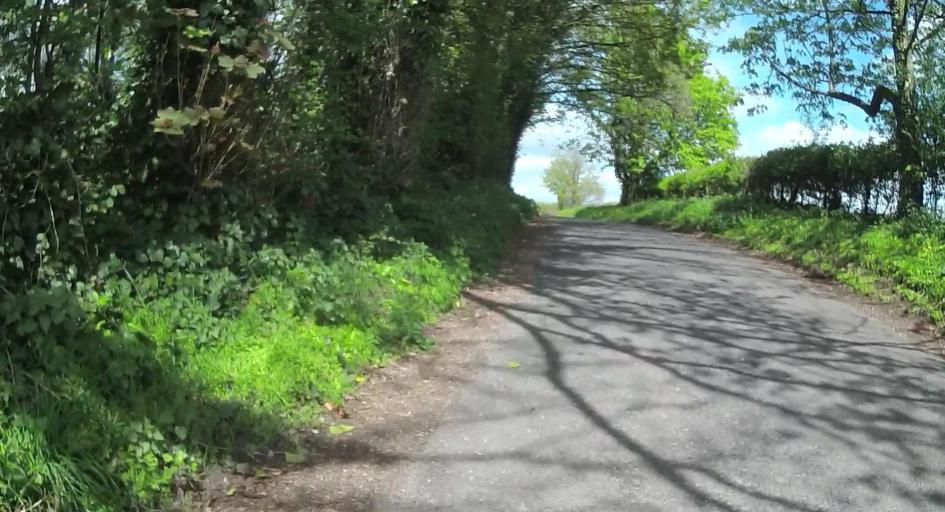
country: GB
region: England
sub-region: Hampshire
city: East Dean
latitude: 51.0655
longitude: -1.5321
